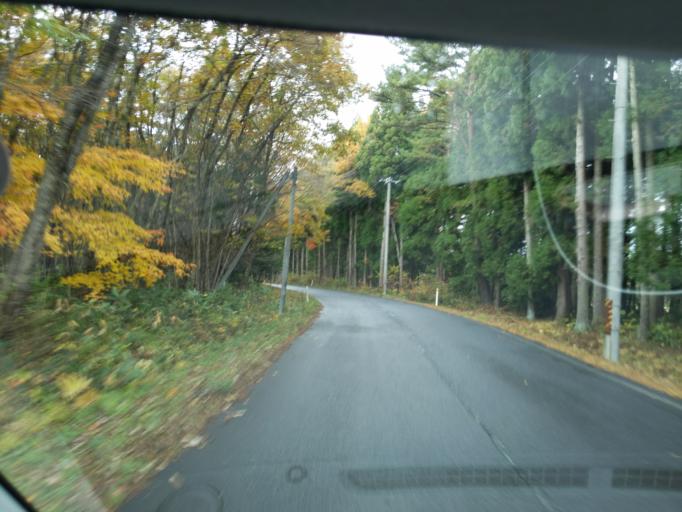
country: JP
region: Iwate
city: Mizusawa
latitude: 39.1027
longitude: 140.9937
